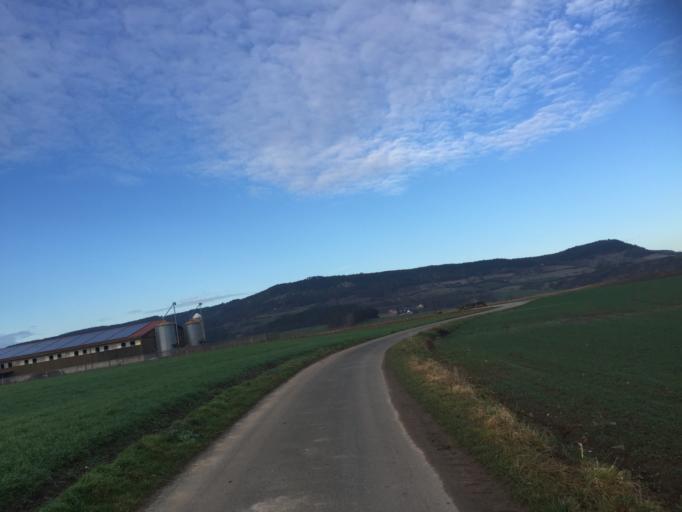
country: DE
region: Thuringia
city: Orlamunde
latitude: 50.7605
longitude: 11.4999
